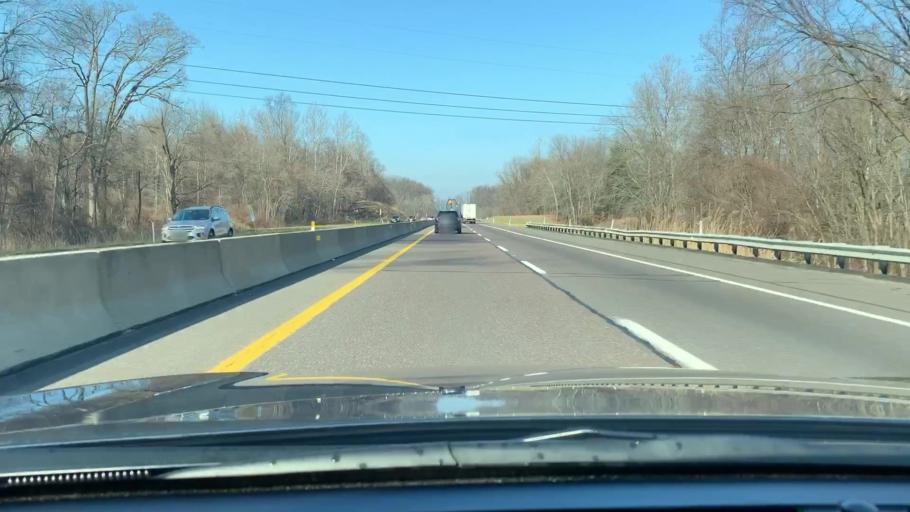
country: US
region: Pennsylvania
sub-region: Chester County
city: Elverson
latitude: 40.1072
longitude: -75.7573
